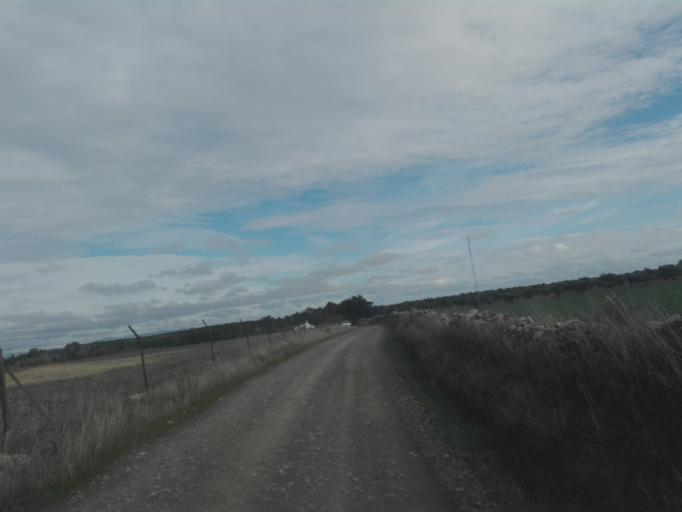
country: ES
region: Extremadura
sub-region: Provincia de Badajoz
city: Villagarcia de la Torre
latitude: 38.3023
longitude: -6.0862
